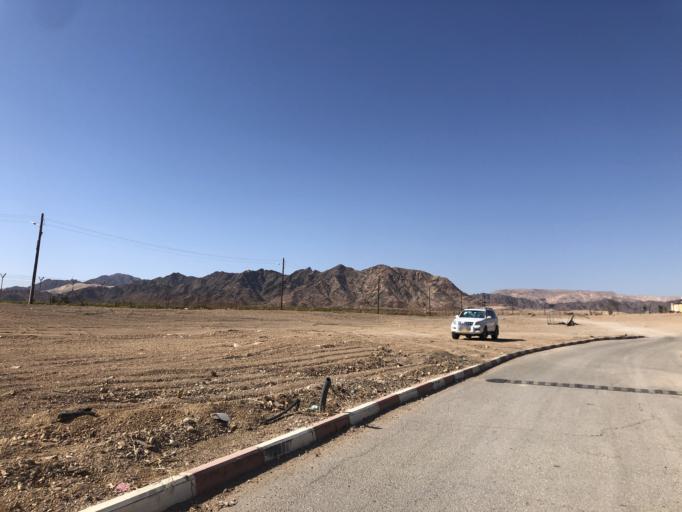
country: IL
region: Southern District
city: Eilat
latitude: 29.5807
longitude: 34.9610
